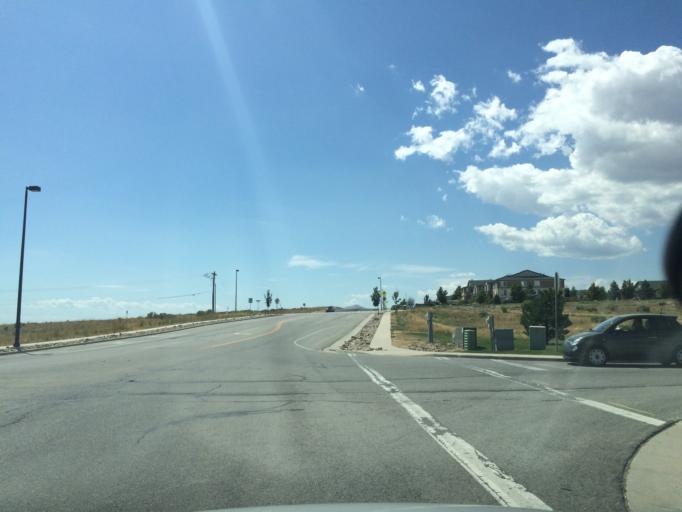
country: US
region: Utah
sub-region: Salt Lake County
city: Oquirrh
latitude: 40.6107
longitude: -112.0507
